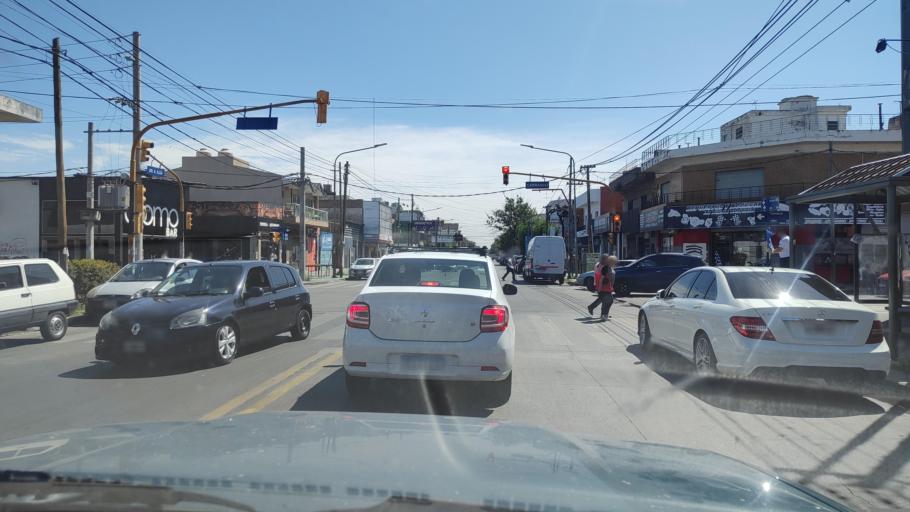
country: AR
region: Buenos Aires
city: San Justo
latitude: -34.6810
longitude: -58.5699
